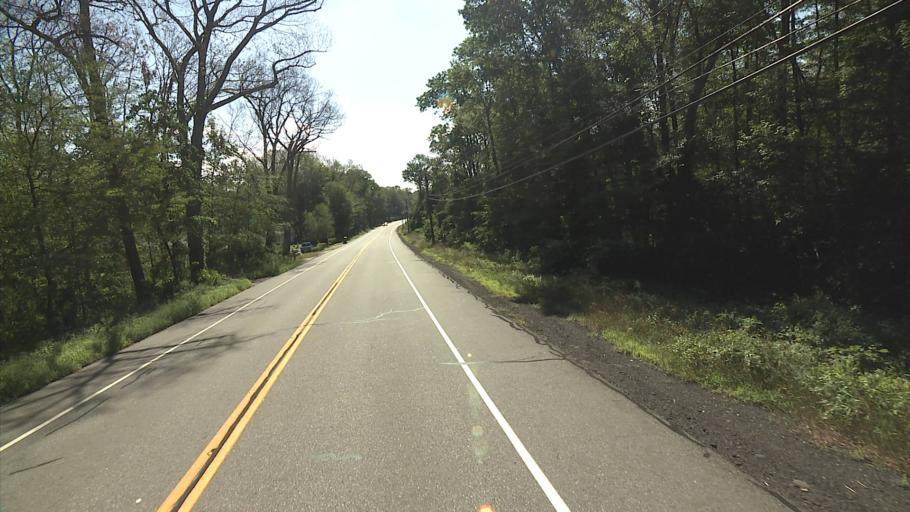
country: US
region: Connecticut
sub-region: Tolland County
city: Crystal Lake
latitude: 41.9755
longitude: -72.3744
